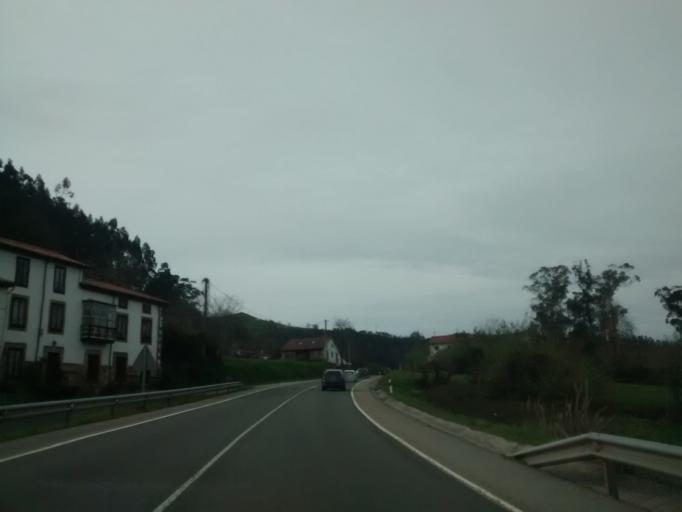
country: ES
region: Cantabria
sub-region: Provincia de Cantabria
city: Puente Viesgo
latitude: 43.2908
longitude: -3.9610
